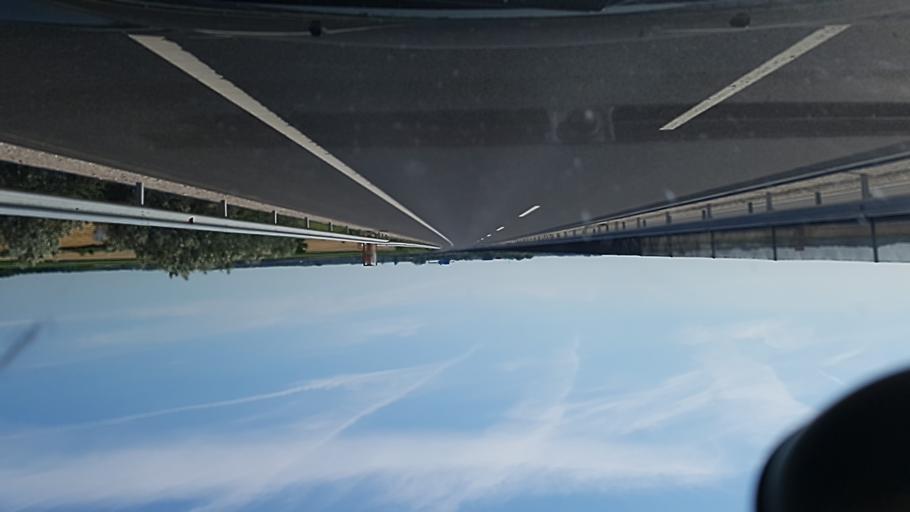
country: HU
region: Tolna
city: Tolna
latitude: 46.3970
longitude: 18.7502
